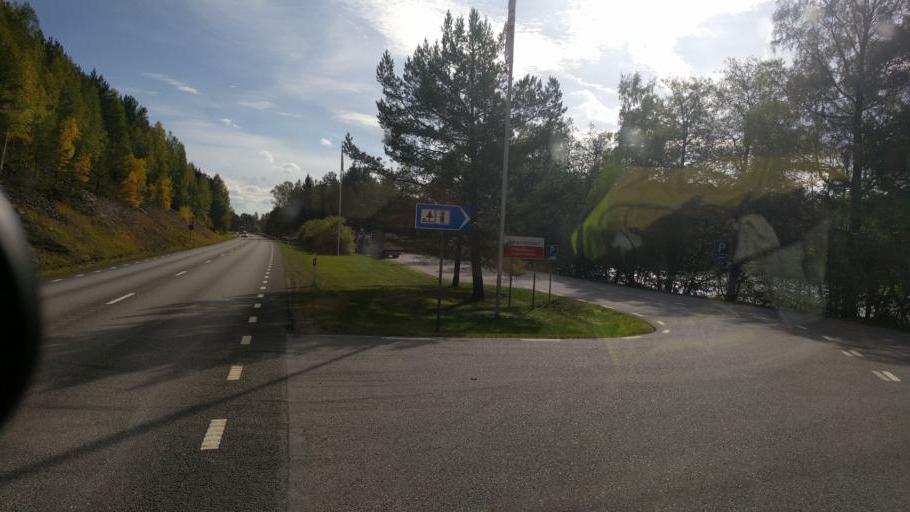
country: SE
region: OEstergoetland
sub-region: Kinda Kommun
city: Kisa
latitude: 57.9347
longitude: 15.6689
